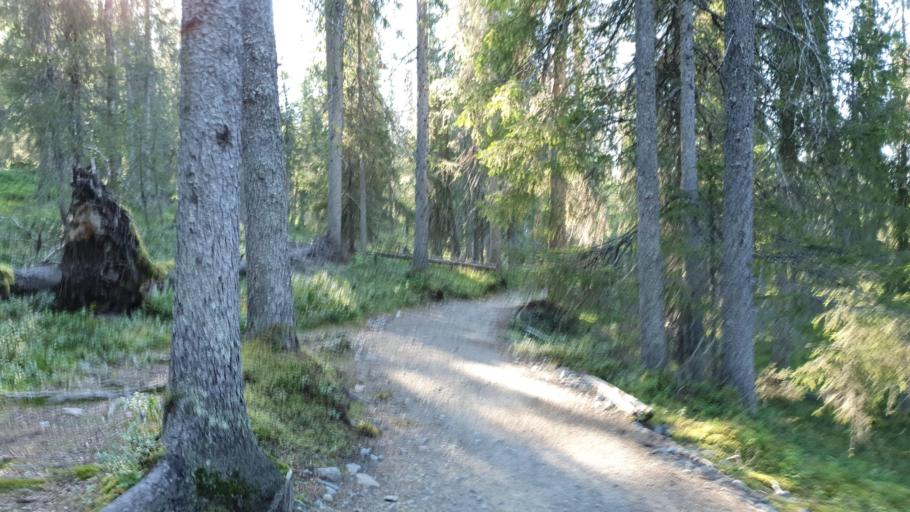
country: FI
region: Lapland
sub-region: Tunturi-Lappi
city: Kolari
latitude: 67.5969
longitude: 24.2277
